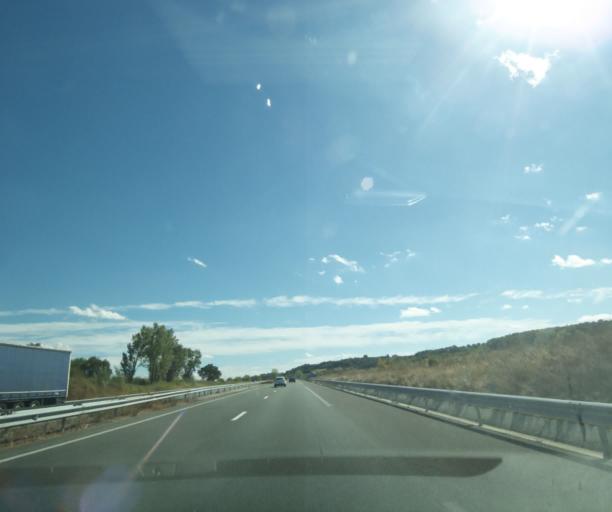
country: FR
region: Aquitaine
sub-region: Departement du Lot-et-Garonne
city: Damazan
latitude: 44.2758
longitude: 0.2728
